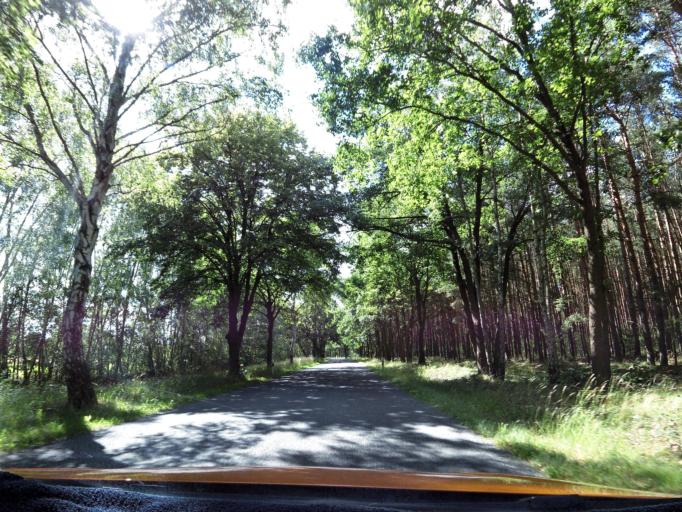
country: DE
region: Brandenburg
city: Erkner
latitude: 52.3188
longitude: 13.7655
